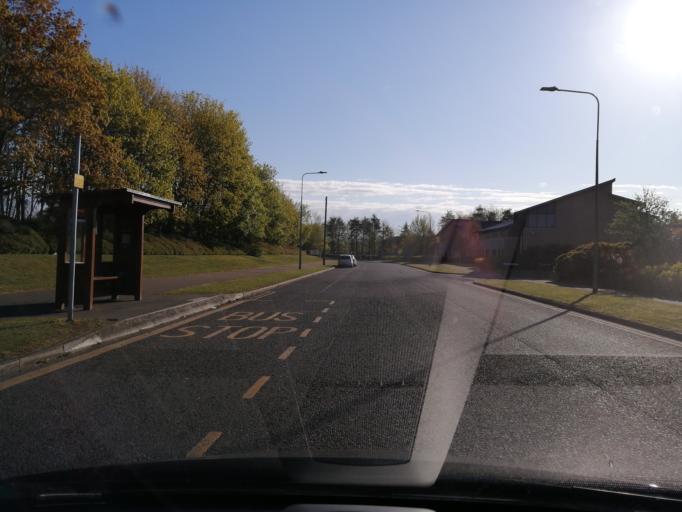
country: GB
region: England
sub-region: Peterborough
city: Castor
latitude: 52.5521
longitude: -0.3208
